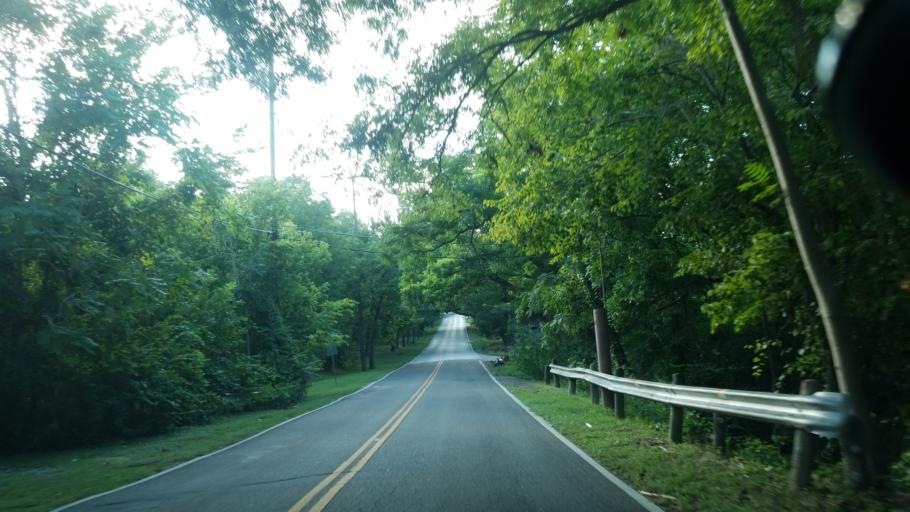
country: US
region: Texas
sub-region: Dallas County
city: Dallas
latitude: 32.7805
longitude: -96.7137
